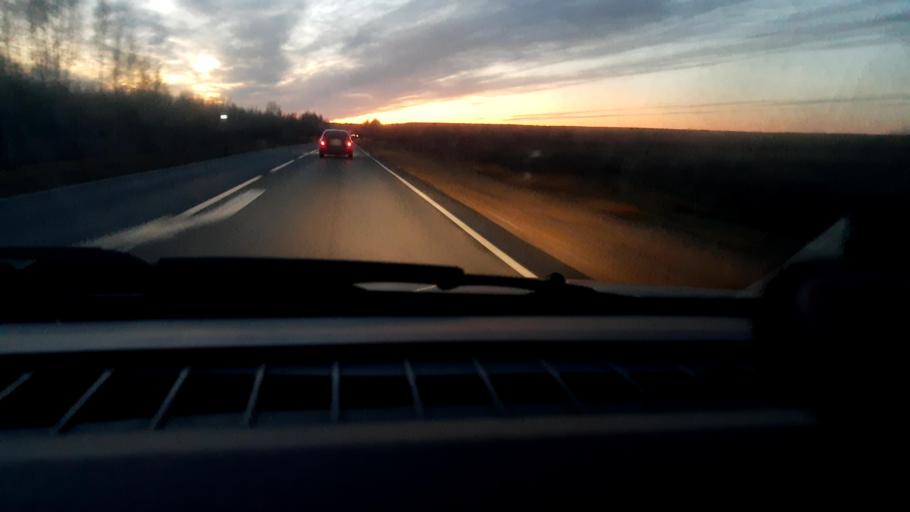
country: RU
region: Nizjnij Novgorod
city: Sukhobezvodnoye
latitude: 56.8599
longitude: 44.8659
